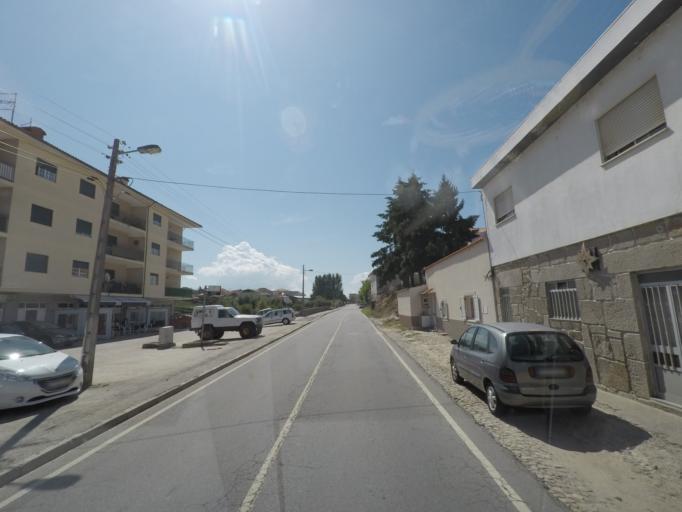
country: PT
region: Vila Real
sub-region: Sabrosa
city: Sabrosa
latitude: 41.2670
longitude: -7.4795
